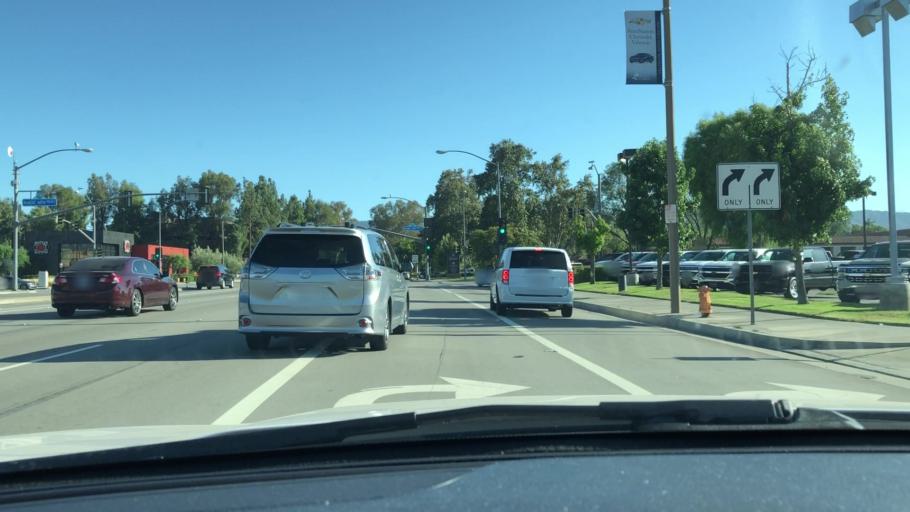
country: US
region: California
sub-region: Los Angeles County
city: Santa Clarita
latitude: 34.4168
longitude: -118.5496
